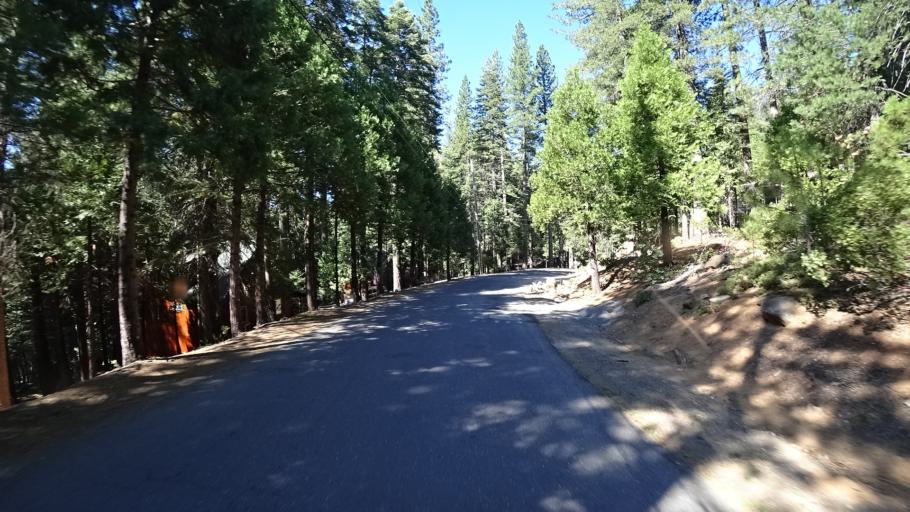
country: US
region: California
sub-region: Calaveras County
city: Arnold
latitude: 38.2954
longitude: -120.2764
